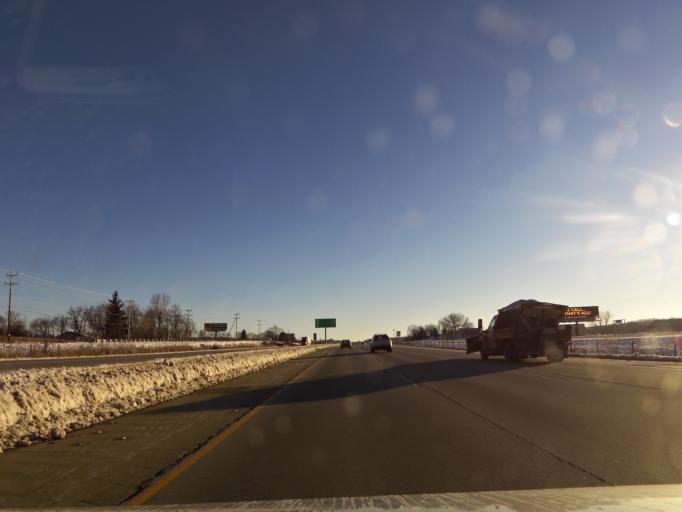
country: US
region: Wisconsin
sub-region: Racine County
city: Caledonia
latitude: 42.8212
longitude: -87.9529
